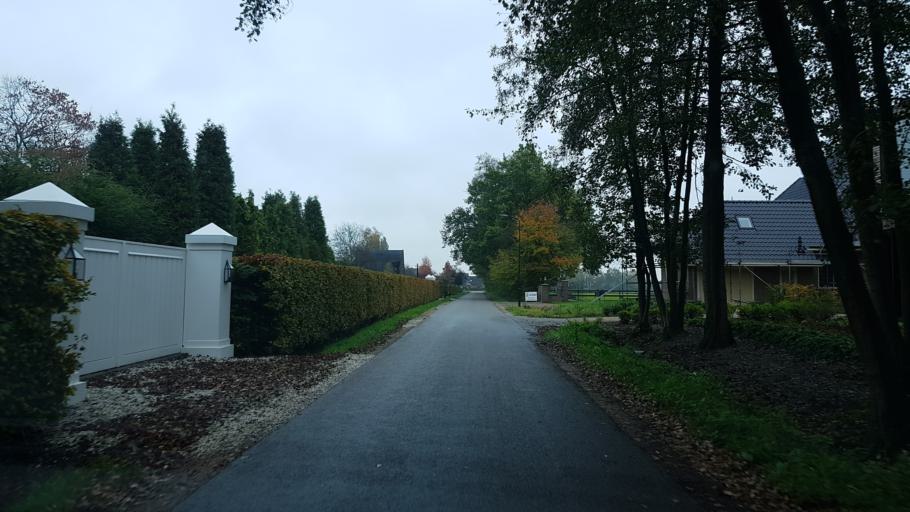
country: NL
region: Gelderland
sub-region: Gemeente Epe
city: Vaassen
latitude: 52.2496
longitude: 5.9579
